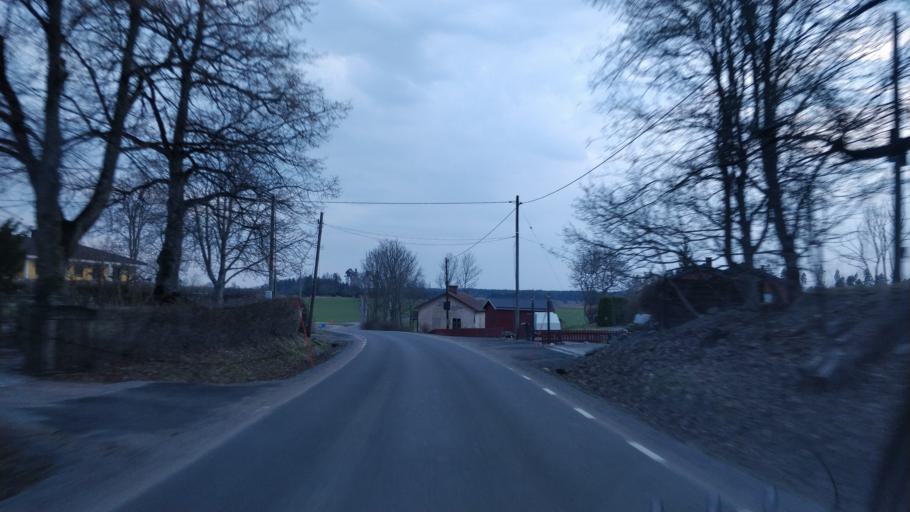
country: SE
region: Uppsala
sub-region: Enkopings Kommun
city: Orsundsbro
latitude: 59.7228
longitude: 17.2682
